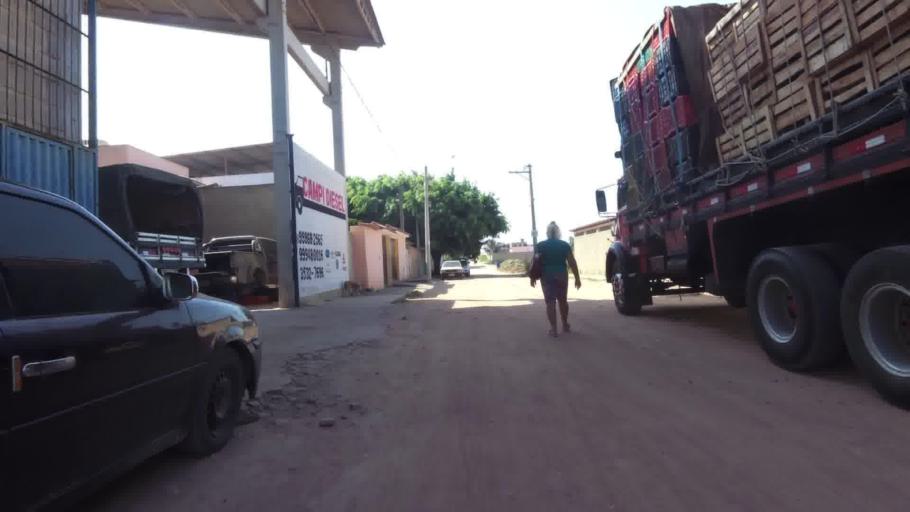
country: BR
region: Espirito Santo
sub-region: Marataizes
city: Marataizes
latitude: -21.0450
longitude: -40.8424
